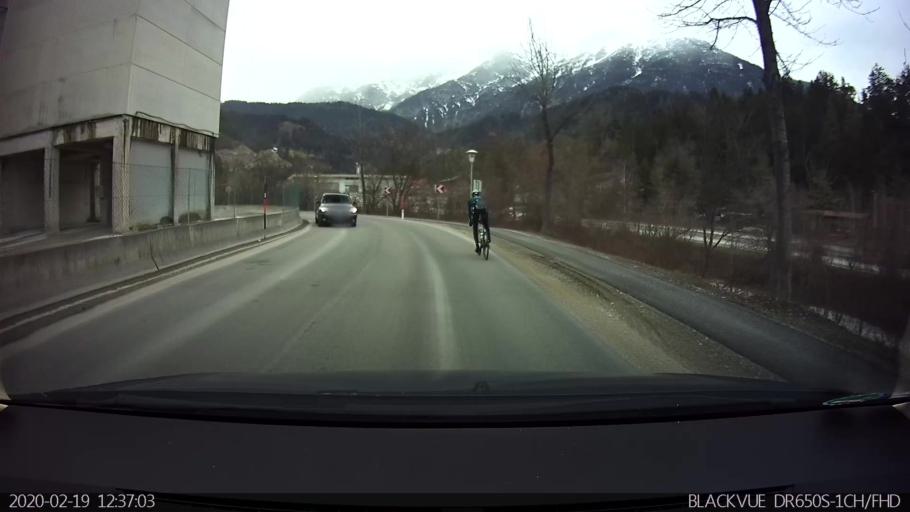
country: AT
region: Tyrol
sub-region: Politischer Bezirk Schwaz
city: Vomp
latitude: 47.3307
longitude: 11.6675
